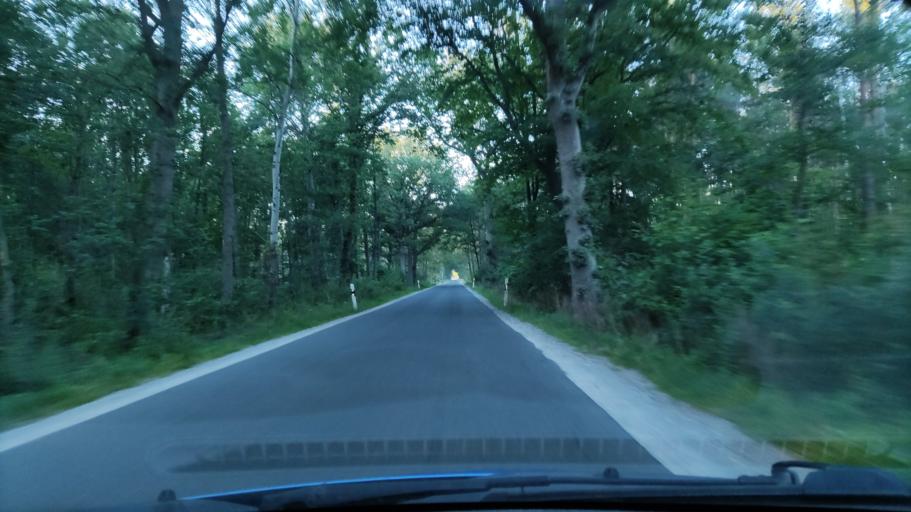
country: DE
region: Lower Saxony
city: Klein Gusborn
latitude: 53.0578
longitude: 11.1823
